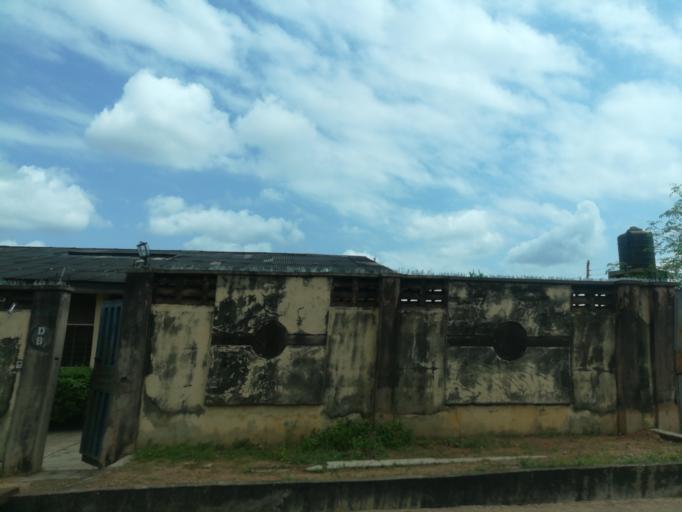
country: NG
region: Oyo
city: Egbeda
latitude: 7.4192
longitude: 4.0000
